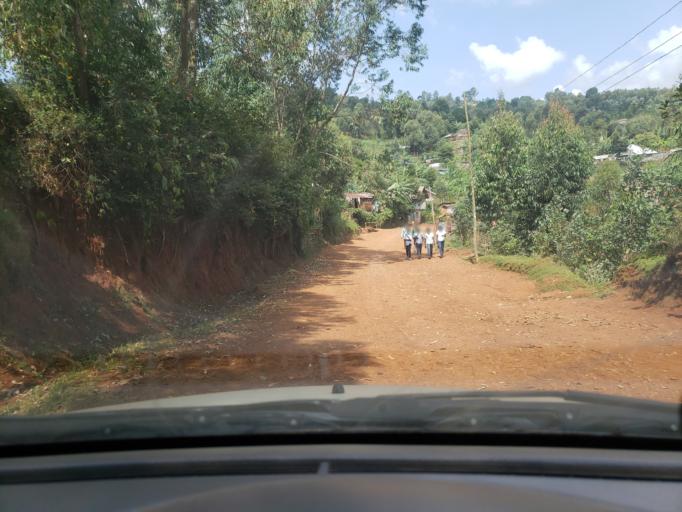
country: CD
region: South Kivu
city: Bukavu
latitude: -2.5073
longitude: 28.8266
